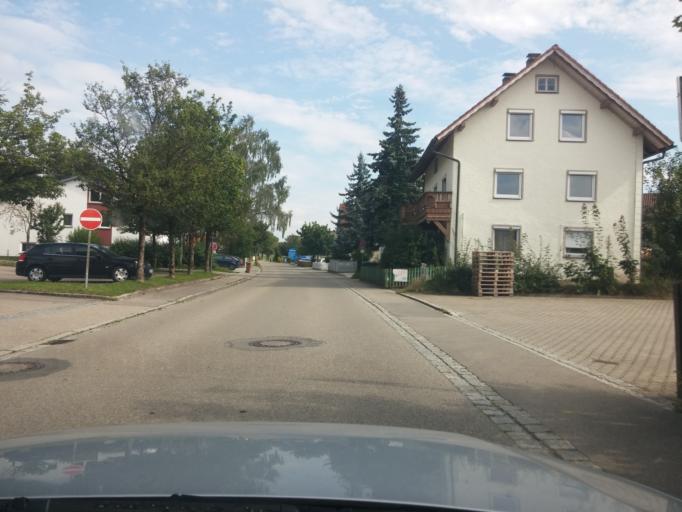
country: DE
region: Bavaria
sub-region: Swabia
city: Legau
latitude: 47.8552
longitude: 10.1321
